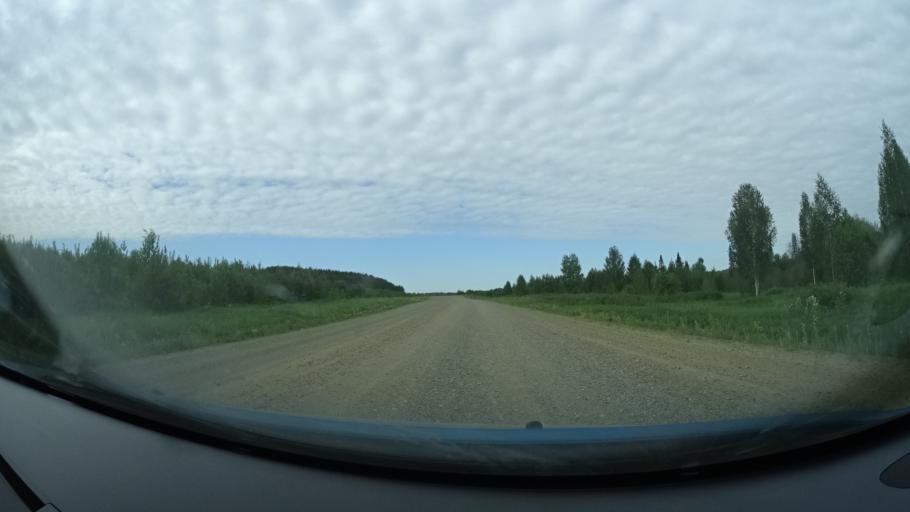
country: RU
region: Perm
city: Kuyeda
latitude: 56.5262
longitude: 55.6319
